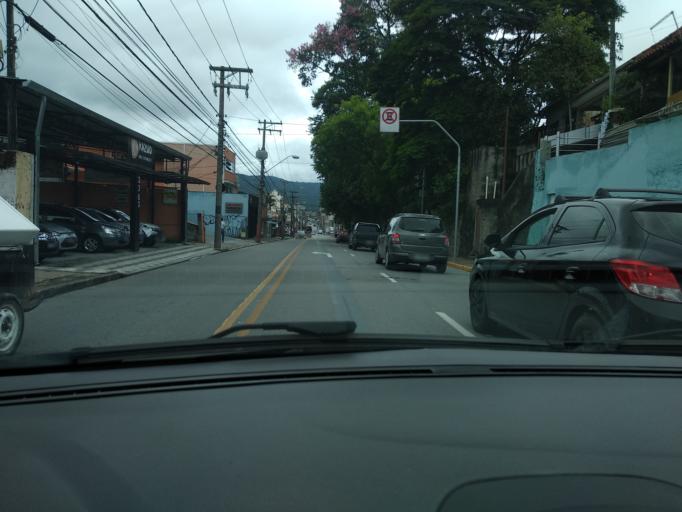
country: BR
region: Sao Paulo
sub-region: Mogi das Cruzes
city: Mogi das Cruzes
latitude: -23.5320
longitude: -46.1936
